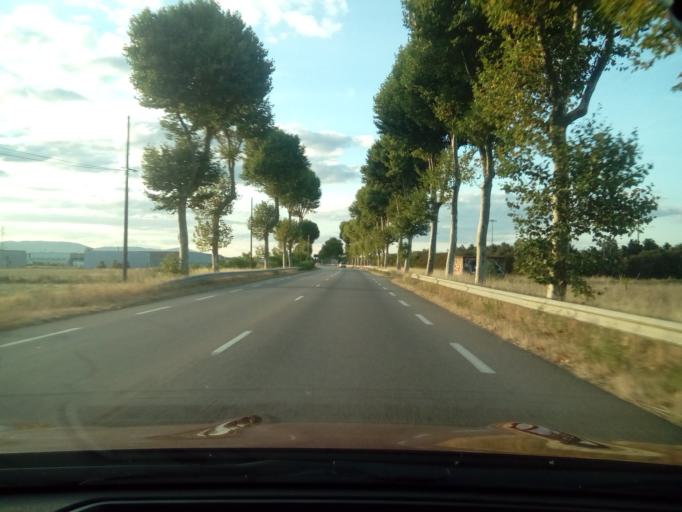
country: FR
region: Rhone-Alpes
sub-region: Departement de la Drome
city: Andancette
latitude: 45.2731
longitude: 4.8236
